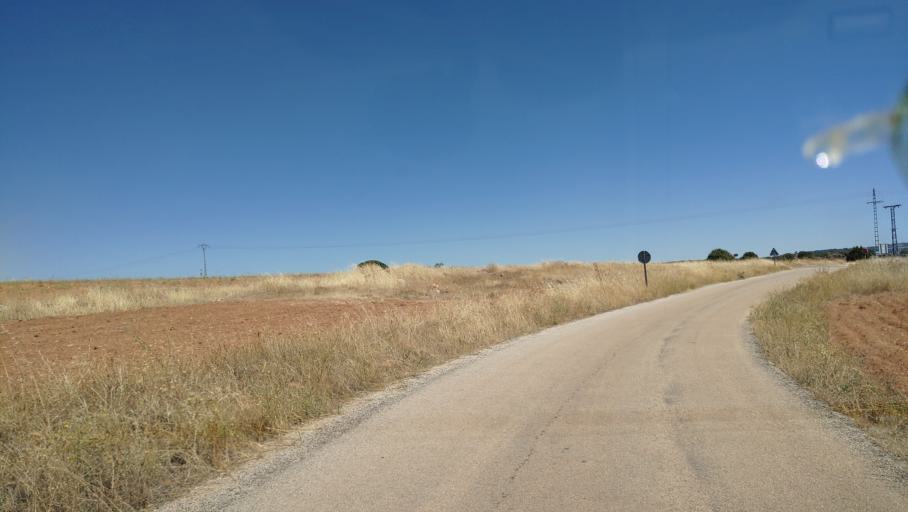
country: ES
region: Castille-La Mancha
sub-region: Provincia de Albacete
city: Ossa de Montiel
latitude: 38.9353
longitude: -2.7536
